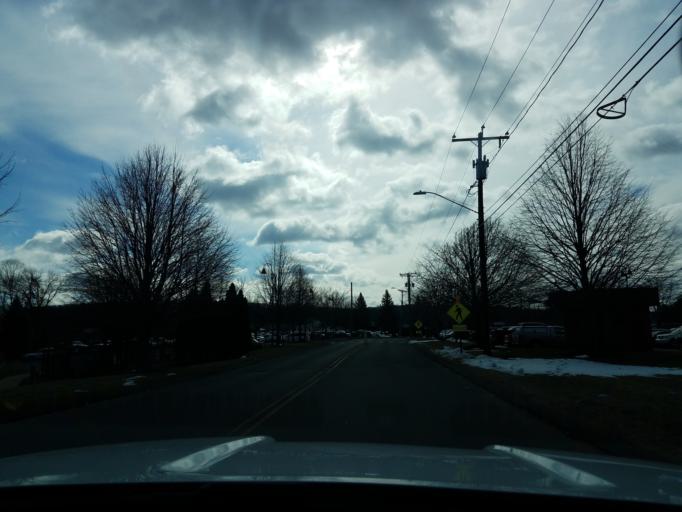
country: US
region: Connecticut
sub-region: Hartford County
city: Plainville
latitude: 41.6422
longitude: -72.8768
